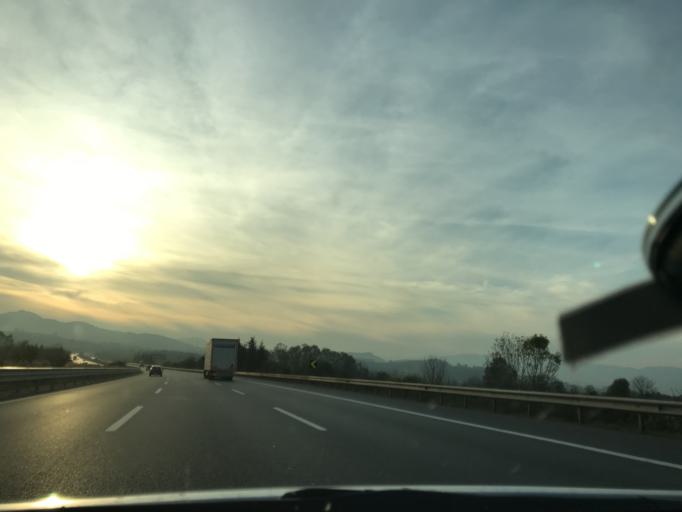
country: TR
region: Duzce
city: Cumayeri
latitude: 40.8449
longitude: 31.0044
